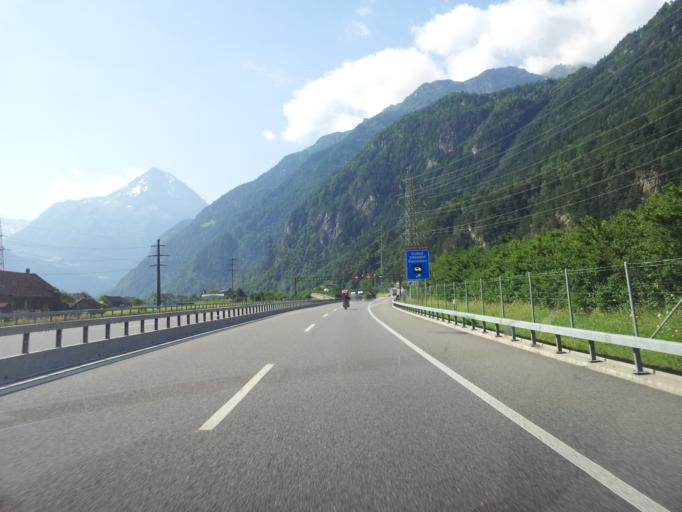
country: CH
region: Uri
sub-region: Uri
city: Erstfeld
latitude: 46.8391
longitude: 8.6370
